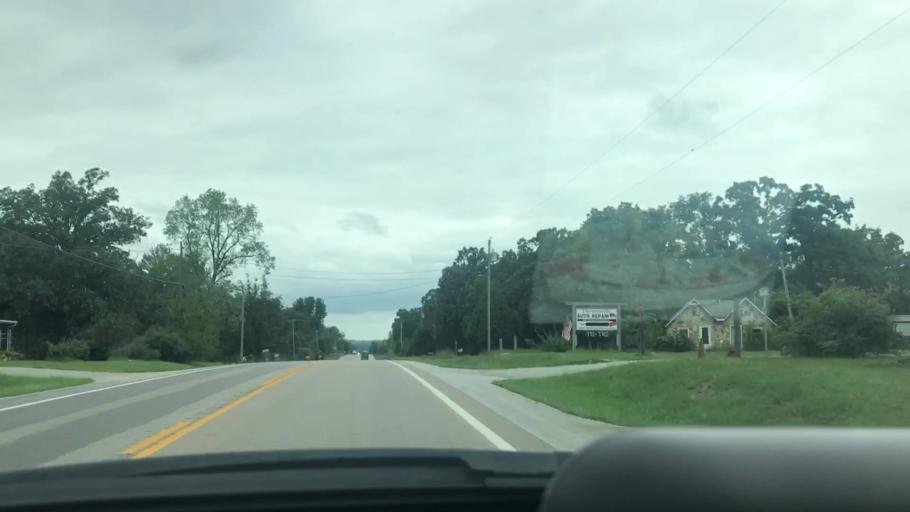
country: US
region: Missouri
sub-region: Dallas County
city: Buffalo
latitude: 37.7028
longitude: -93.1087
